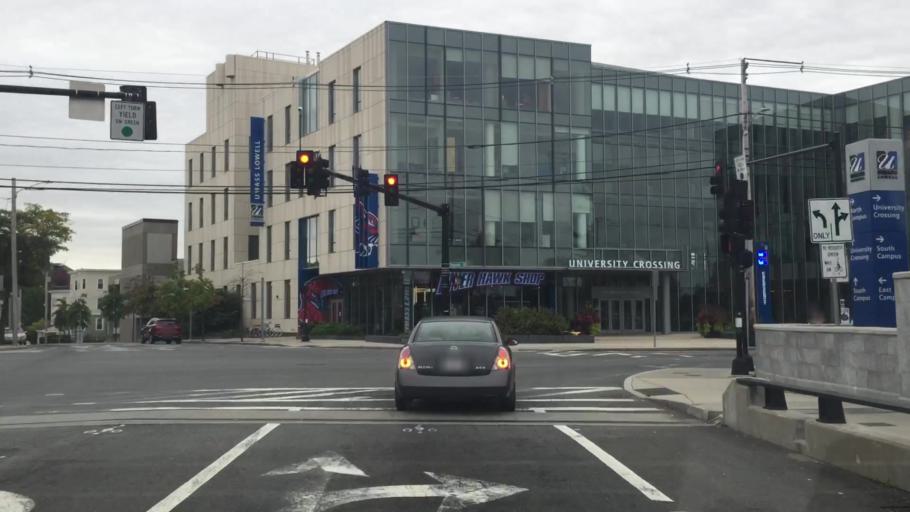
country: US
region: Massachusetts
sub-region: Middlesex County
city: Lowell
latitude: 42.6509
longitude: -71.3242
